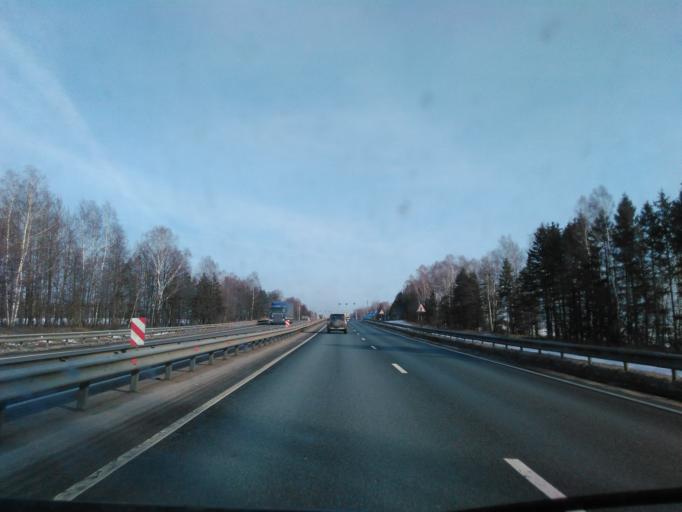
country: RU
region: Smolensk
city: Verkhnedneprovskiy
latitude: 55.1822
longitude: 33.5425
